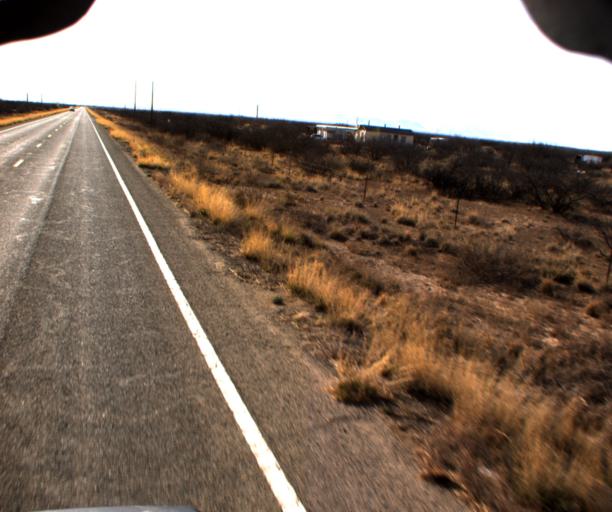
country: US
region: Arizona
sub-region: Cochise County
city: Willcox
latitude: 32.1953
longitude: -109.7402
